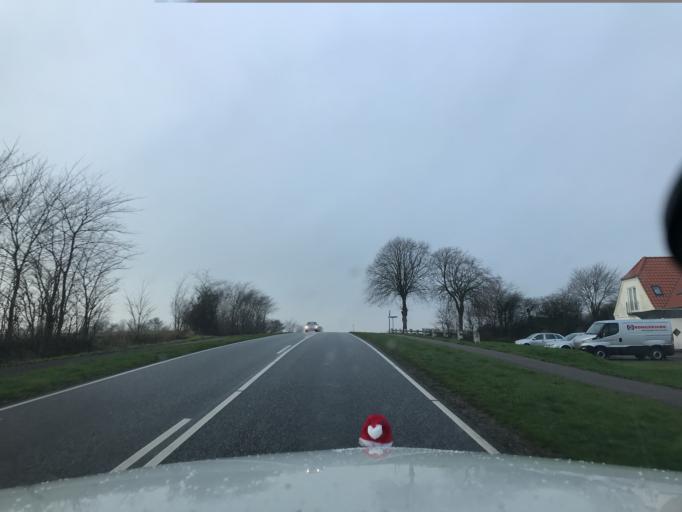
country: DK
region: South Denmark
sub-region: Sonderborg Kommune
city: Dybbol
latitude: 54.9087
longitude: 9.7282
